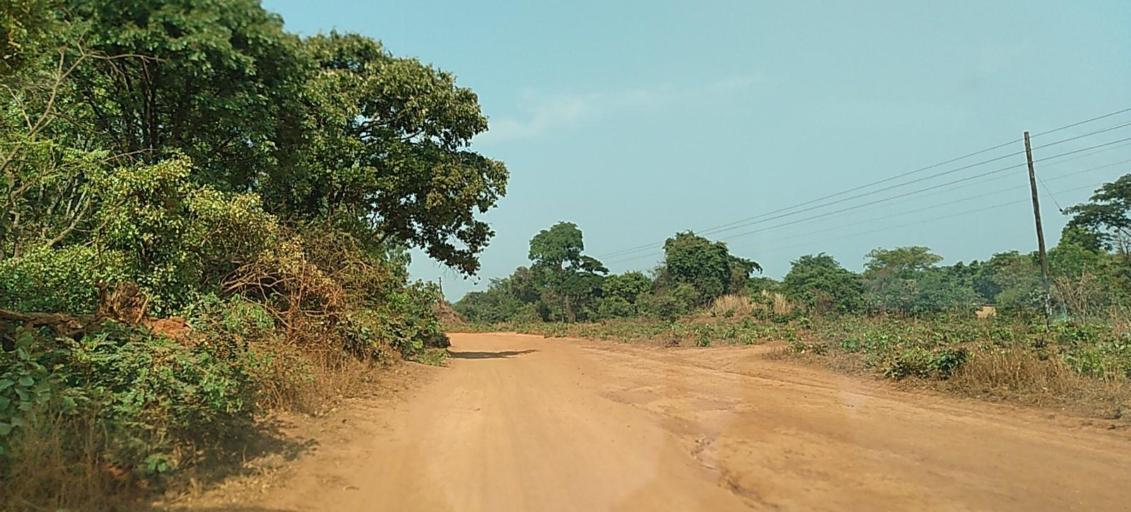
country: ZM
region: Copperbelt
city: Chingola
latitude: -13.0452
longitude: 27.4350
